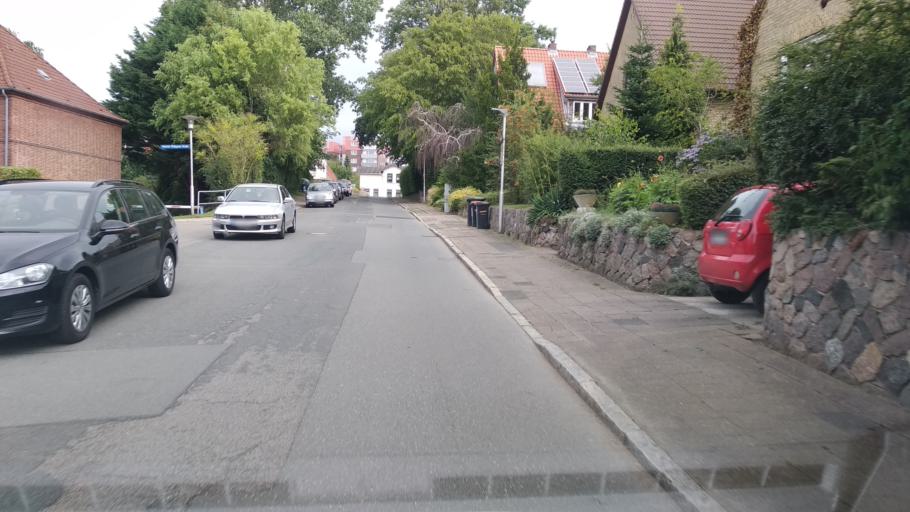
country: DE
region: Schleswig-Holstein
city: Schleswig
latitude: 54.5195
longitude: 9.5754
